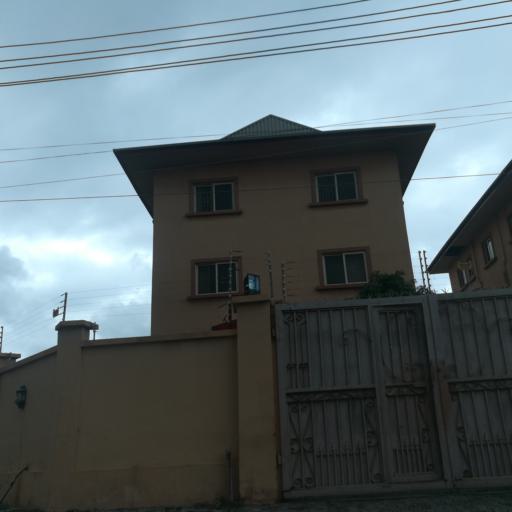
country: NG
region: Lagos
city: Ikoyi
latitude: 6.4404
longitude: 3.4632
